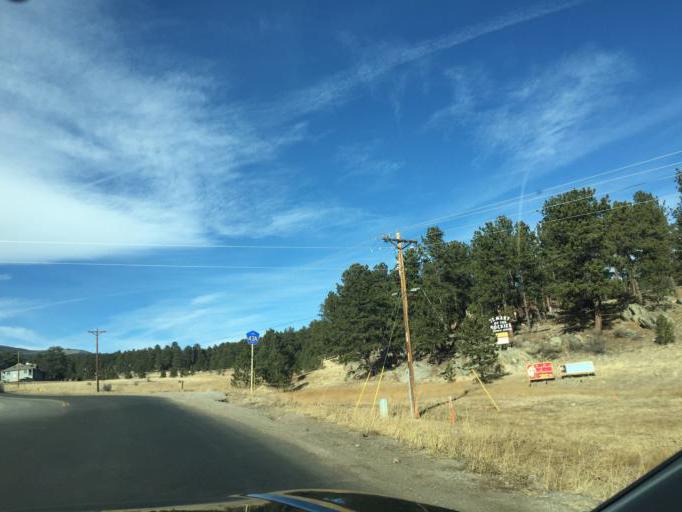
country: US
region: Colorado
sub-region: Jefferson County
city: Evergreen
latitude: 39.4404
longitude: -105.4533
